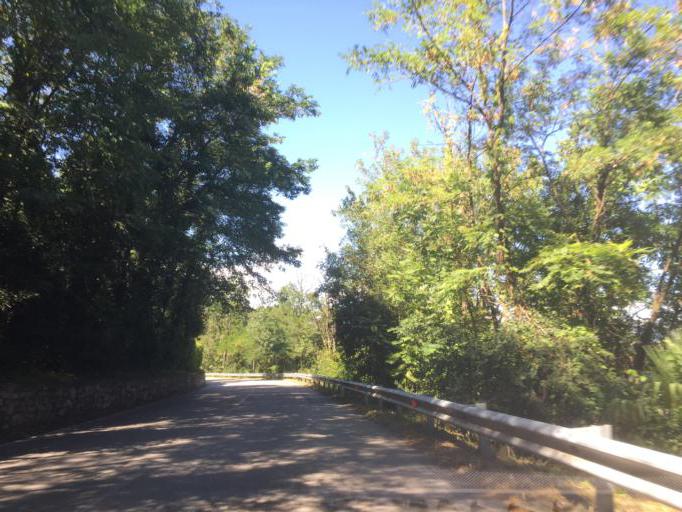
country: IT
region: Lombardy
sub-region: Provincia di Varese
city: Brusimpiano
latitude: 45.9285
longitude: 8.8894
